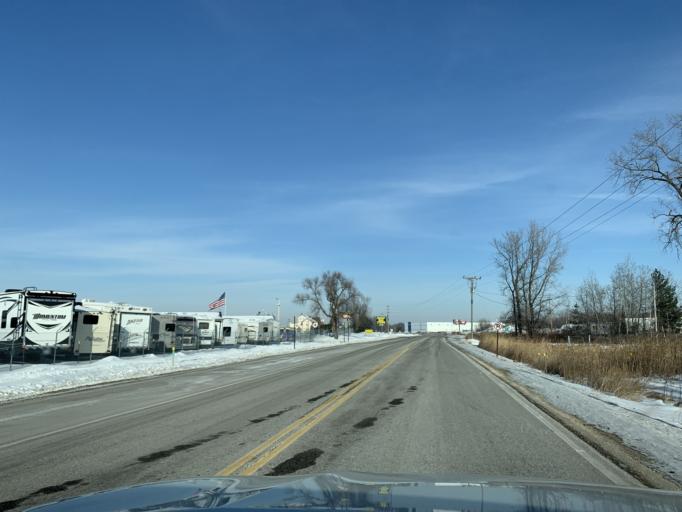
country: US
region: Minnesota
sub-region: Anoka County
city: Columbus
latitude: 45.2308
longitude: -93.0310
